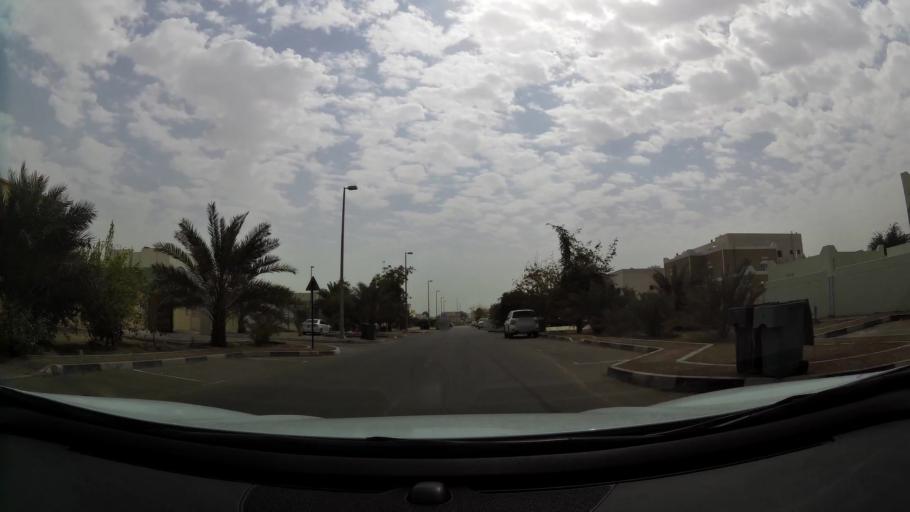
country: AE
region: Abu Dhabi
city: Abu Dhabi
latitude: 24.3087
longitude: 54.6381
